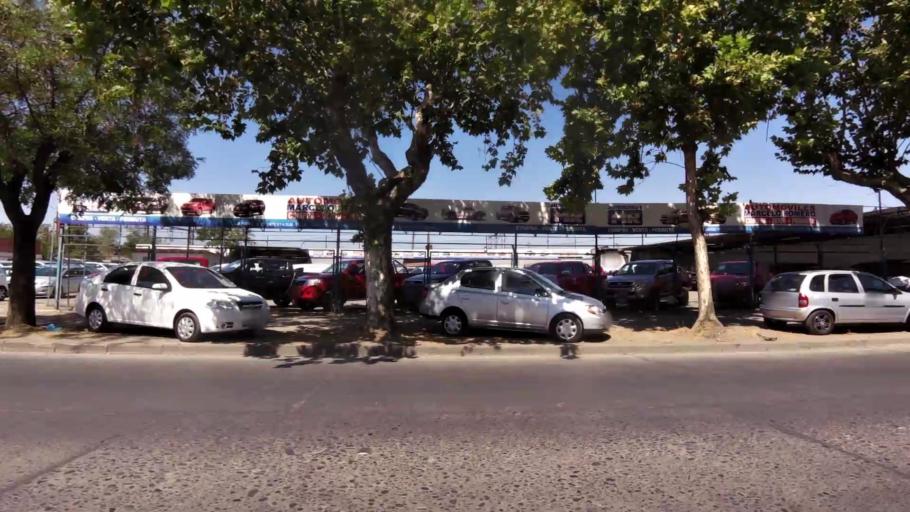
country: CL
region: Maule
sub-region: Provincia de Talca
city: Talca
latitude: -35.4312
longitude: -71.6507
